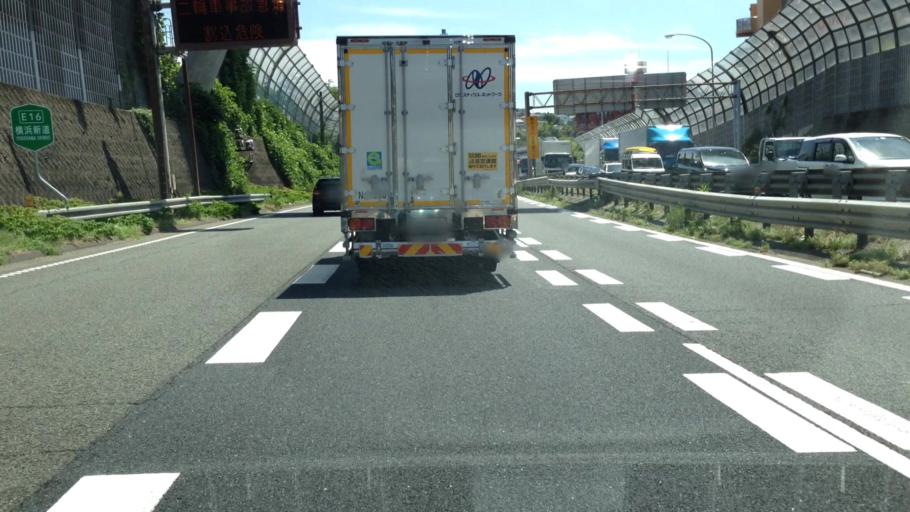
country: JP
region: Kanagawa
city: Yokohama
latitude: 35.4474
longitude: 139.5743
